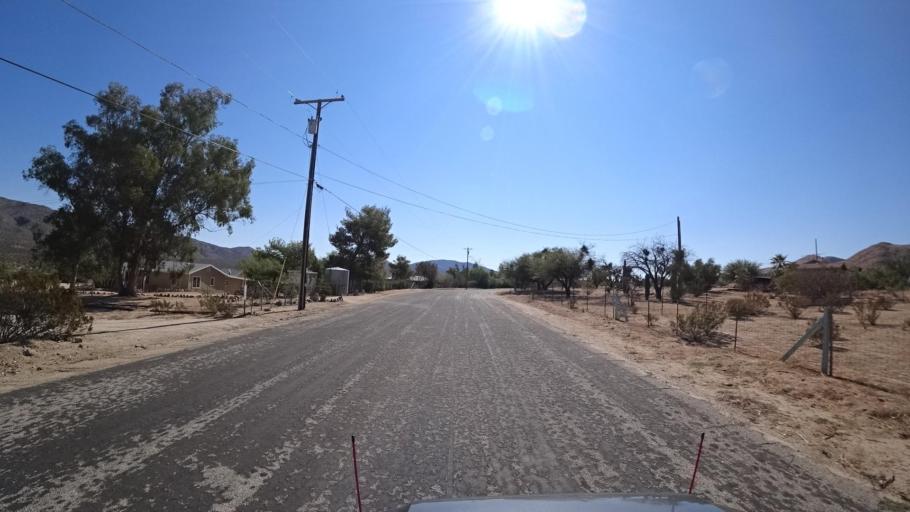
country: US
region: California
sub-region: San Diego County
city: Julian
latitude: 33.0739
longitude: -116.4417
